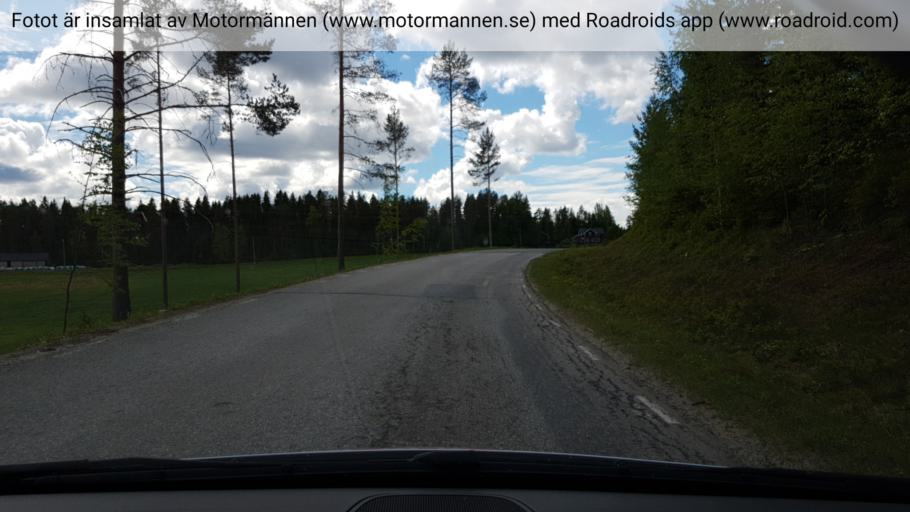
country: SE
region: Vaesterbotten
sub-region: Umea Kommun
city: Roback
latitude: 64.0215
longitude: 20.0862
